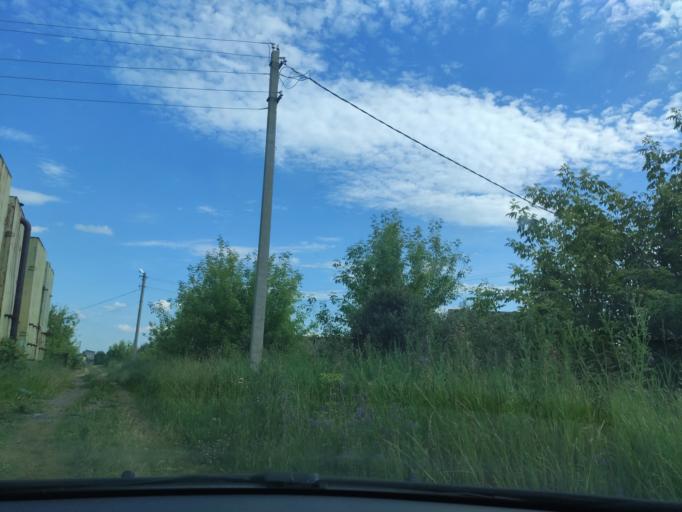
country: RU
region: Ulyanovsk
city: Cherdakly
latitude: 54.4435
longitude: 48.8950
